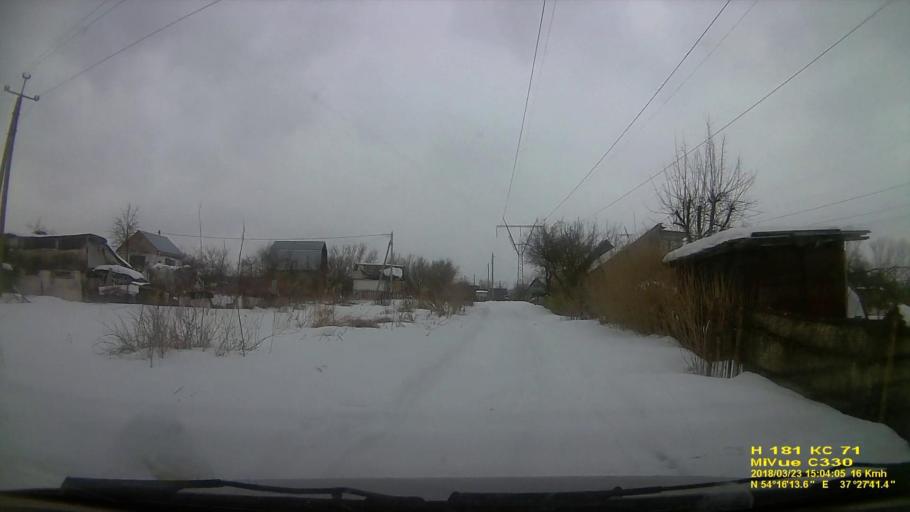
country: RU
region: Tula
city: Leninskiy
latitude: 54.2705
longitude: 37.4615
